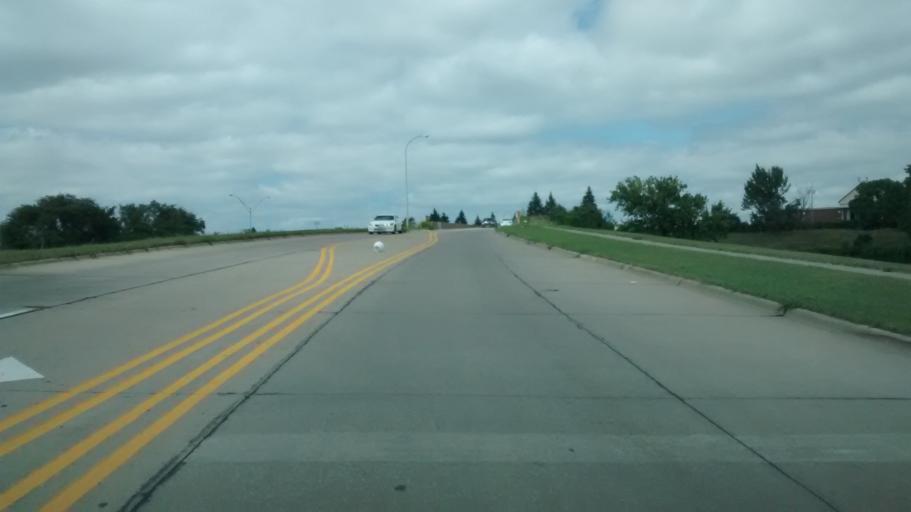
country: US
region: Iowa
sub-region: Woodbury County
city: Sergeant Bluff
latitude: 42.4423
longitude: -96.3524
